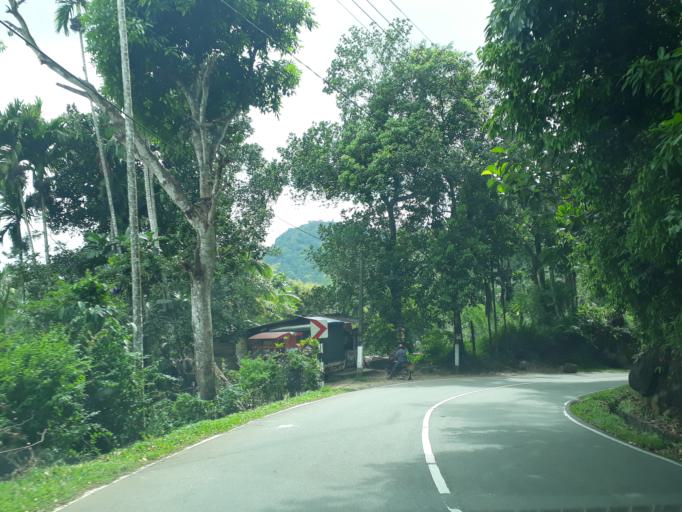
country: LK
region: Southern
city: Weligama
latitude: 6.3196
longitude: 80.5447
